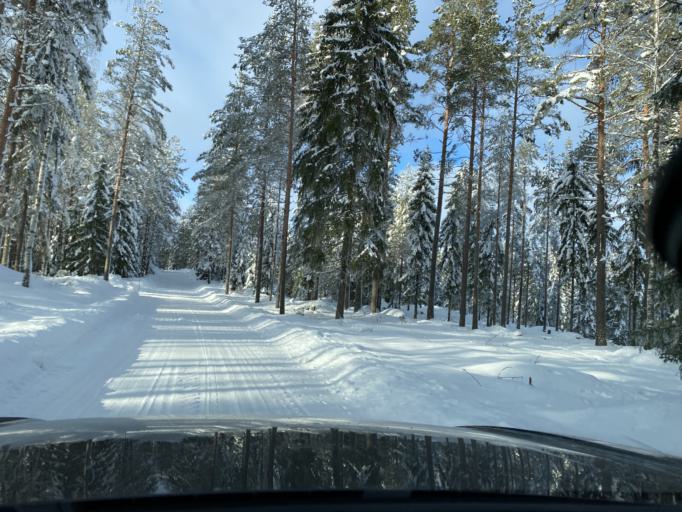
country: FI
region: Pirkanmaa
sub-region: Lounais-Pirkanmaa
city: Punkalaidun
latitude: 61.0725
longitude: 23.2359
